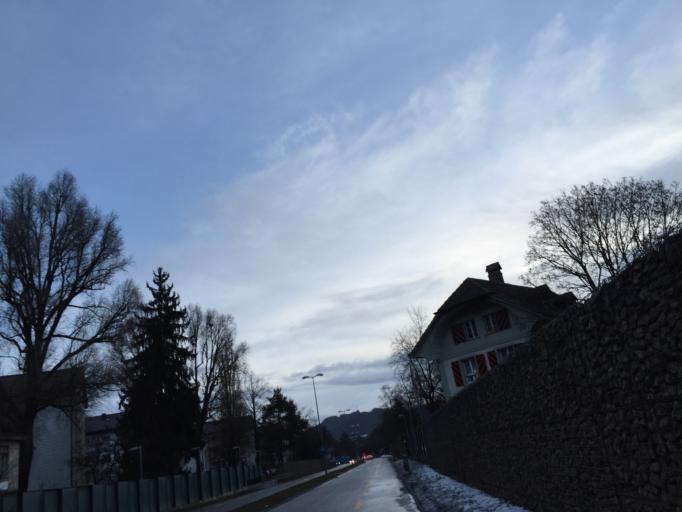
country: CH
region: Bern
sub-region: Bern-Mittelland District
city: Bern
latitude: 46.9719
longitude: 7.4482
